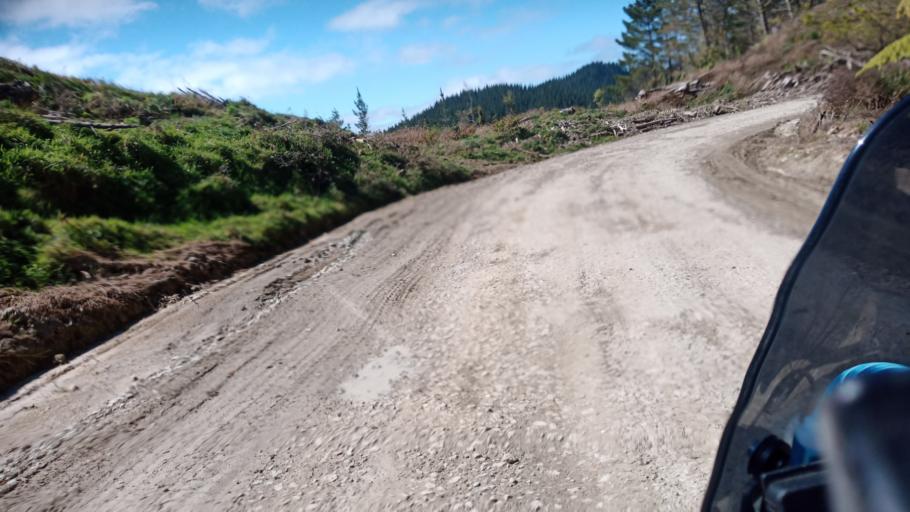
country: NZ
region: Gisborne
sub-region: Gisborne District
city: Gisborne
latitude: -38.8975
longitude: 177.8007
